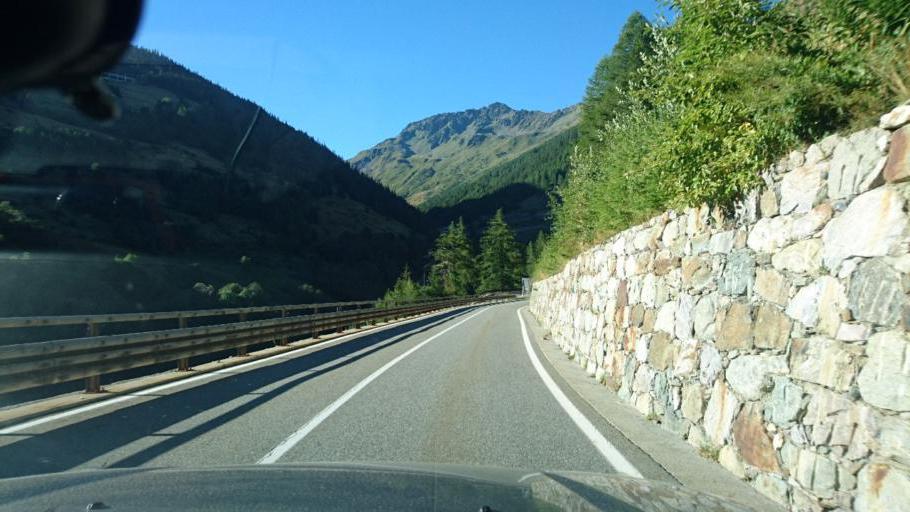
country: IT
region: Aosta Valley
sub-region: Valle d'Aosta
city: San Leonardo
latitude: 45.8259
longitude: 7.1879
